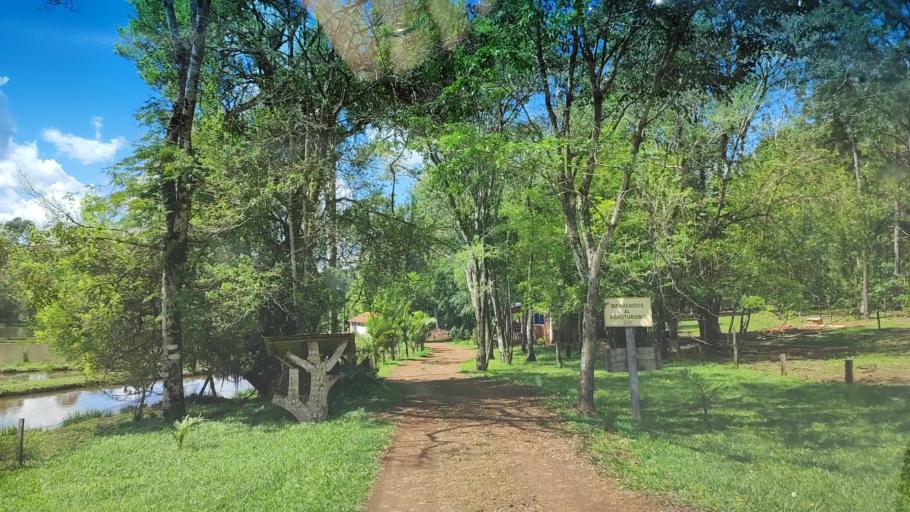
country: AR
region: Misiones
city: Ruiz de Montoya
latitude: -26.9505
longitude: -55.0079
